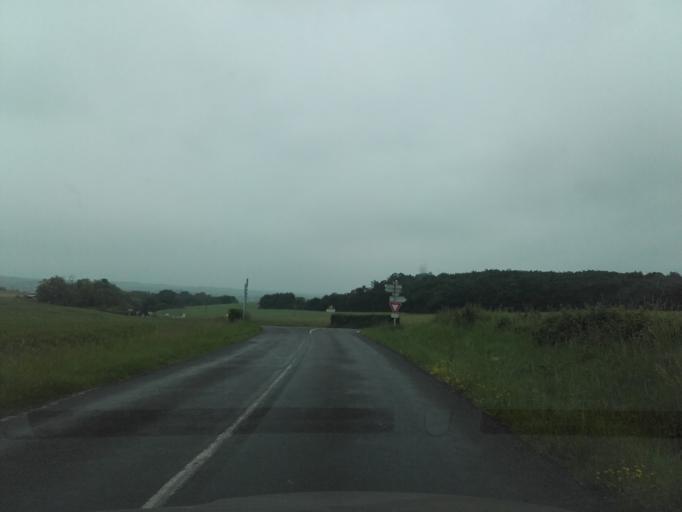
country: FR
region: Centre
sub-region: Departement du Loir-et-Cher
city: Montoire-sur-le-Loir
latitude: 47.7417
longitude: 0.8482
